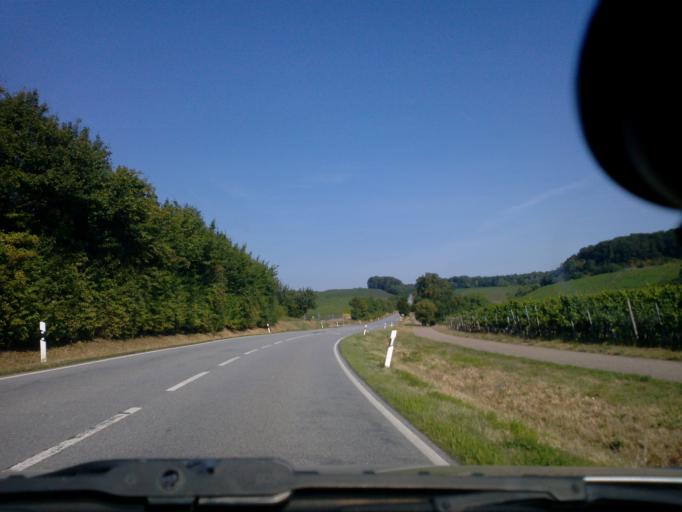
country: DE
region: Baden-Wuerttemberg
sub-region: Regierungsbezirk Stuttgart
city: Brackenheim
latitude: 49.0979
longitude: 9.0308
